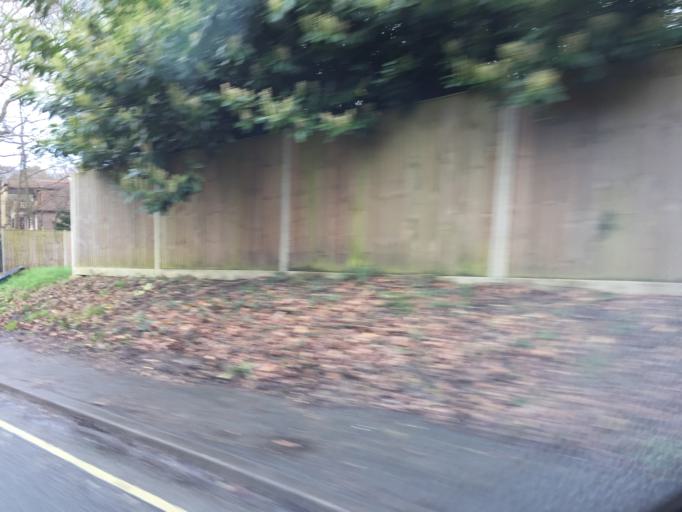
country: GB
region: England
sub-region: Hampshire
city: Eastleigh
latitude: 50.9585
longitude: -1.3994
